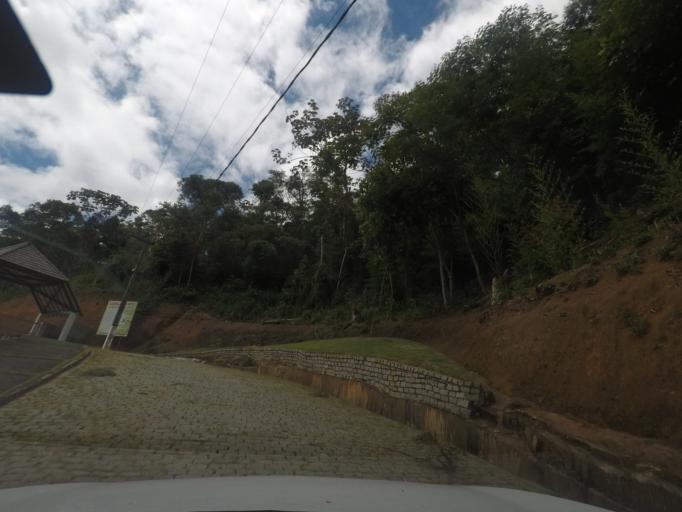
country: BR
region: Rio de Janeiro
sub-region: Teresopolis
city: Teresopolis
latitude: -22.4050
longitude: -42.9837
